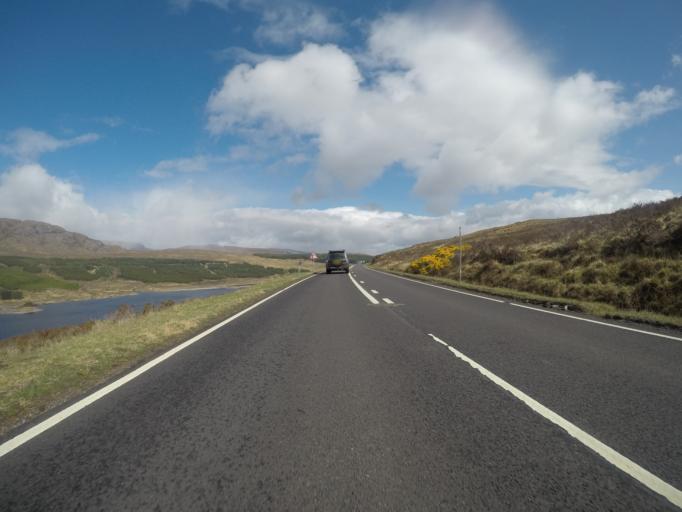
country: GB
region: Scotland
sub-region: Highland
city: Spean Bridge
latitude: 57.1140
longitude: -4.9835
